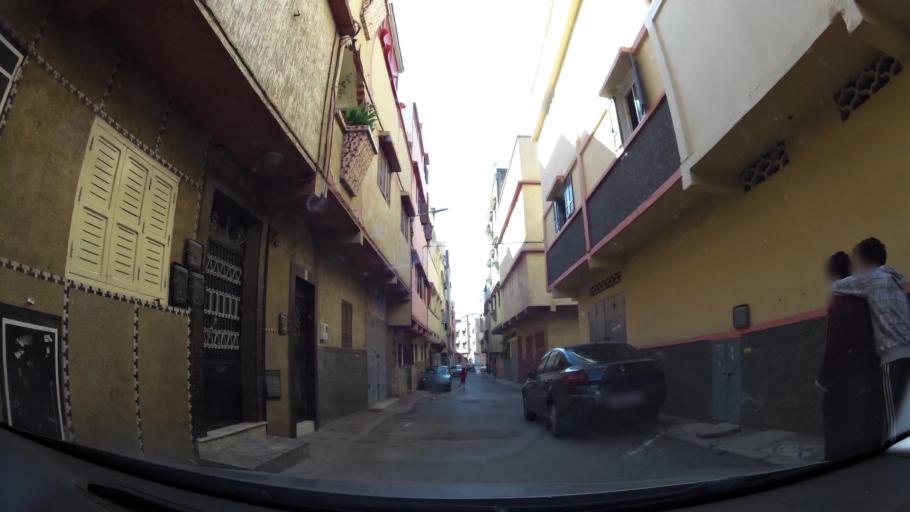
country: MA
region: Rabat-Sale-Zemmour-Zaer
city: Sale
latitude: 34.0448
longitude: -6.8127
